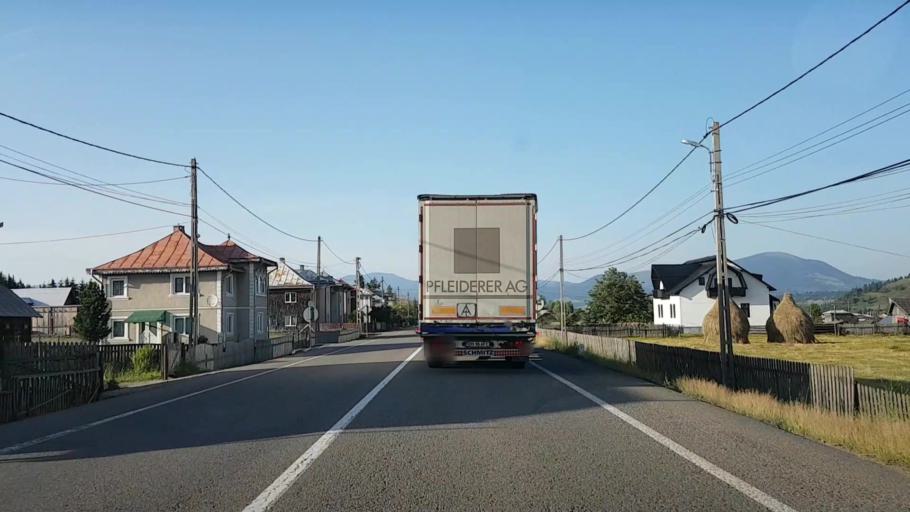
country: RO
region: Suceava
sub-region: Comuna Poiana Stampei
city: Poiana Stampei
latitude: 47.3130
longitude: 25.1303
